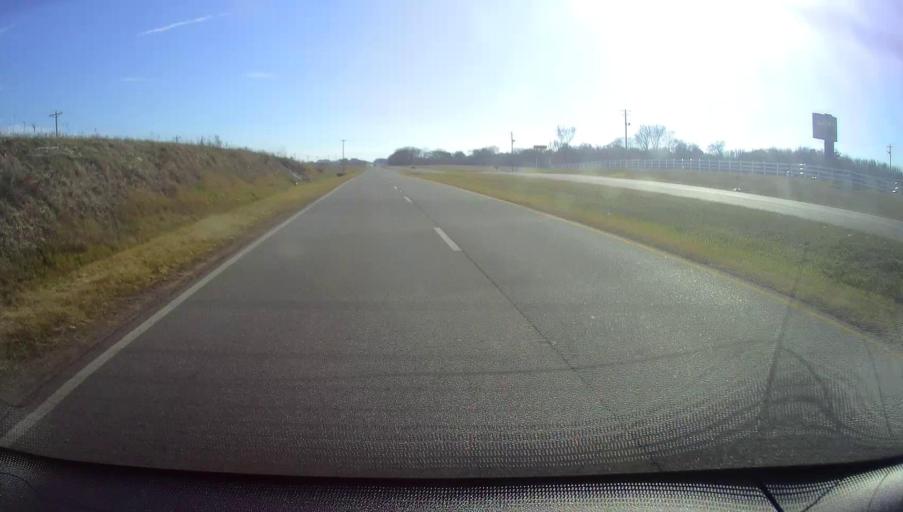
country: US
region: Alabama
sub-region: Morgan County
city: Decatur
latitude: 34.6710
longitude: -86.9500
